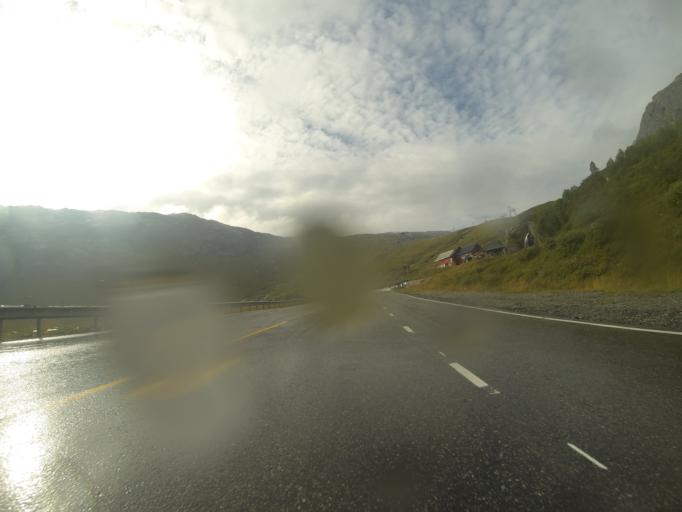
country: NO
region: Hordaland
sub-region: Odda
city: Odda
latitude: 59.8222
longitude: 6.7423
